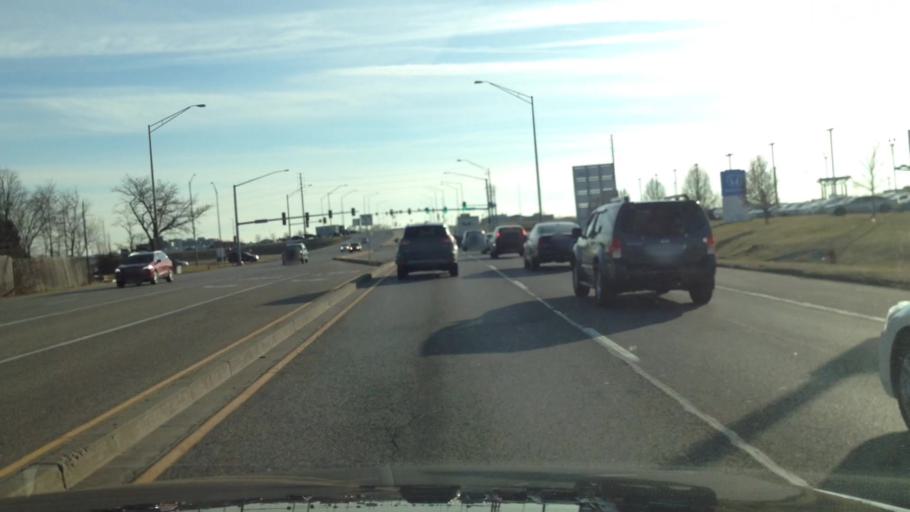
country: US
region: Illinois
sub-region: Kane County
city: Sleepy Hollow
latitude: 42.0849
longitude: -88.3355
